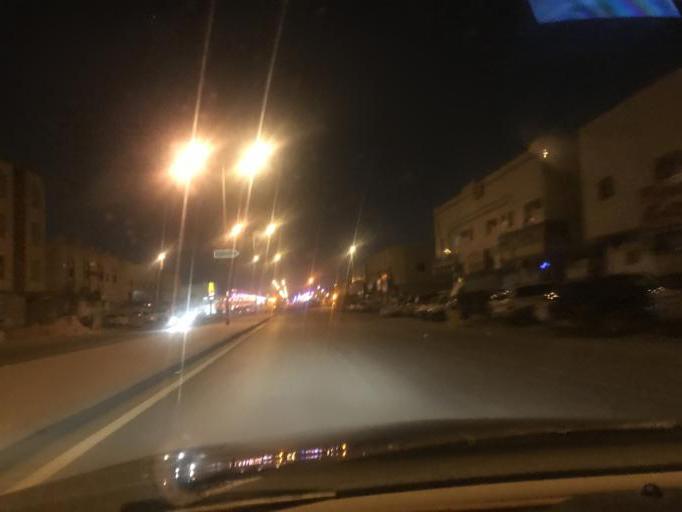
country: SA
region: Ar Riyad
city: Riyadh
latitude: 24.7631
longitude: 46.7973
